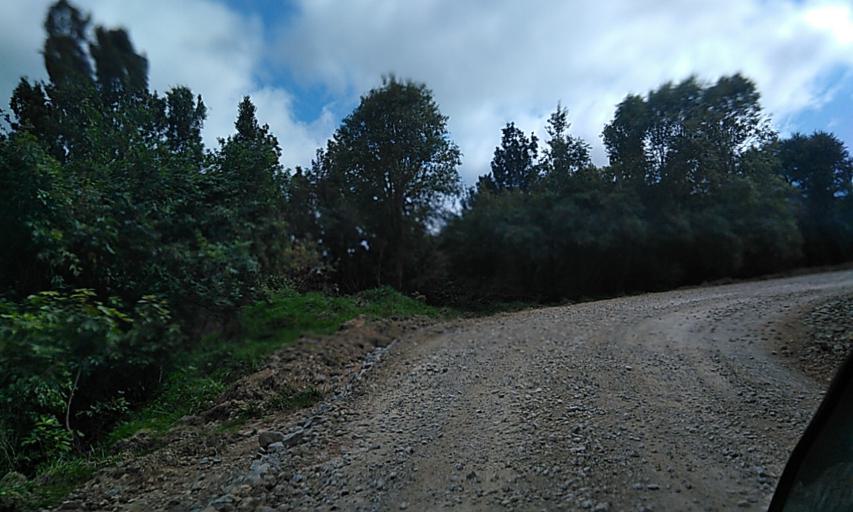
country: NZ
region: Gisborne
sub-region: Gisborne District
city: Gisborne
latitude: -38.3151
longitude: 178.0842
